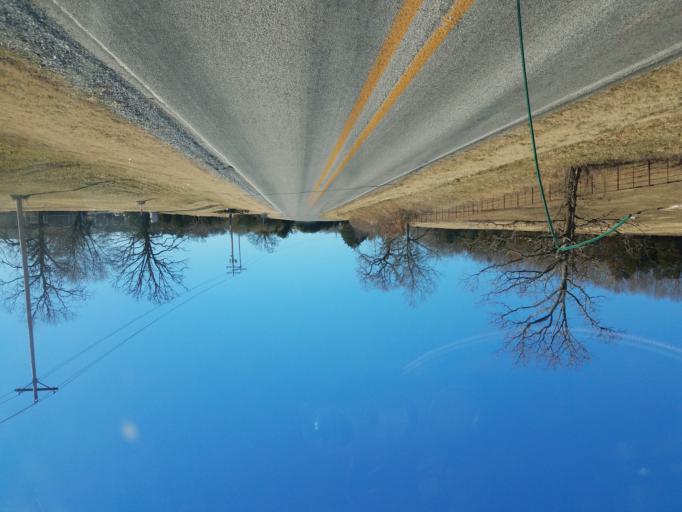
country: US
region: Arkansas
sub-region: Washington County
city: Elkins
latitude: 36.0257
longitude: -93.9932
